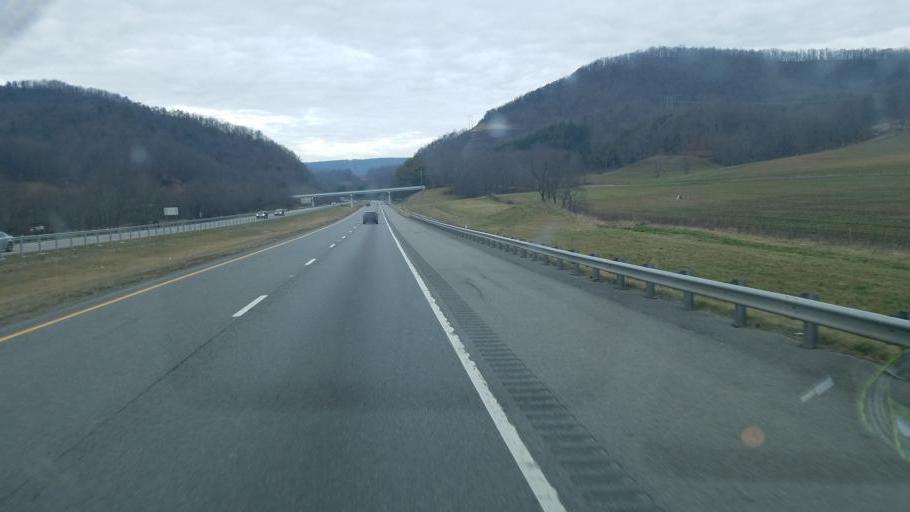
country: US
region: Virginia
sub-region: Wythe County
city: Wytheville
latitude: 36.9837
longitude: -81.0728
